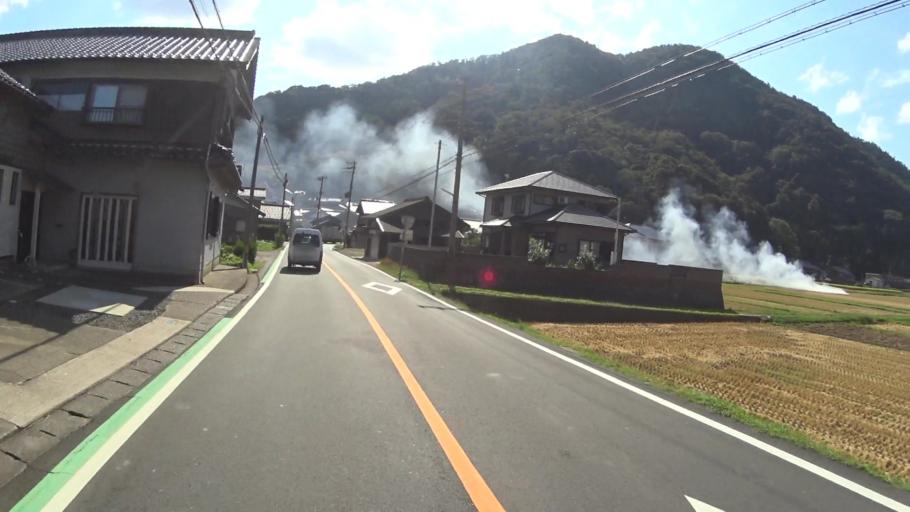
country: JP
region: Kyoto
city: Miyazu
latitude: 35.7481
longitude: 135.1647
